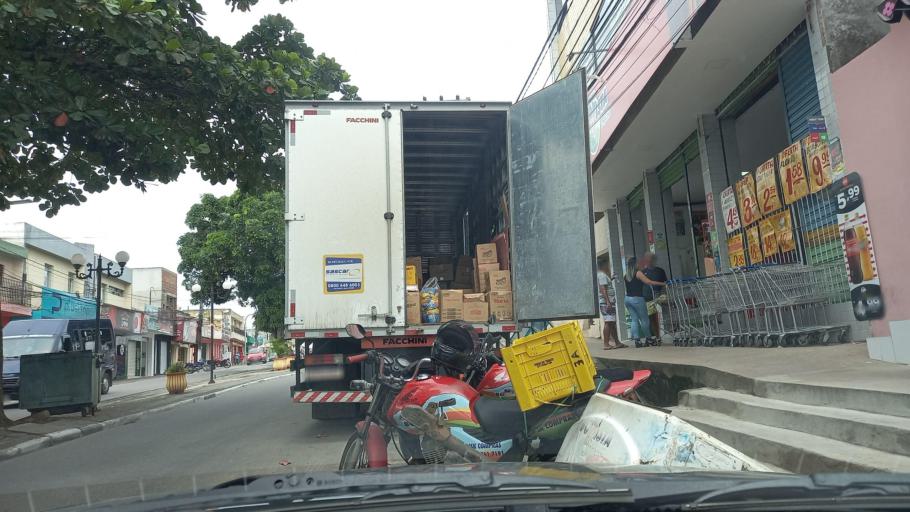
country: BR
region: Pernambuco
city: Garanhuns
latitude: -8.8952
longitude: -36.4951
